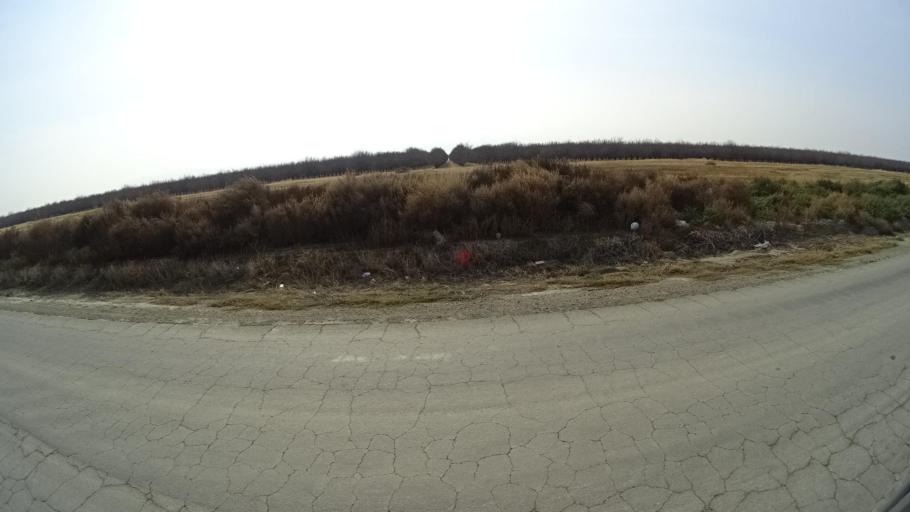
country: US
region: California
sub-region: Kern County
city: Greenfield
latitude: 35.0947
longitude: -119.0872
